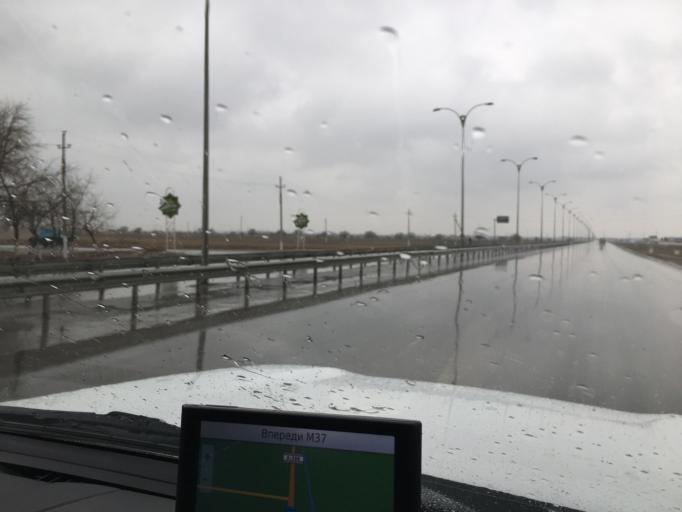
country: TM
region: Mary
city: Mary
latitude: 37.5568
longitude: 61.8548
